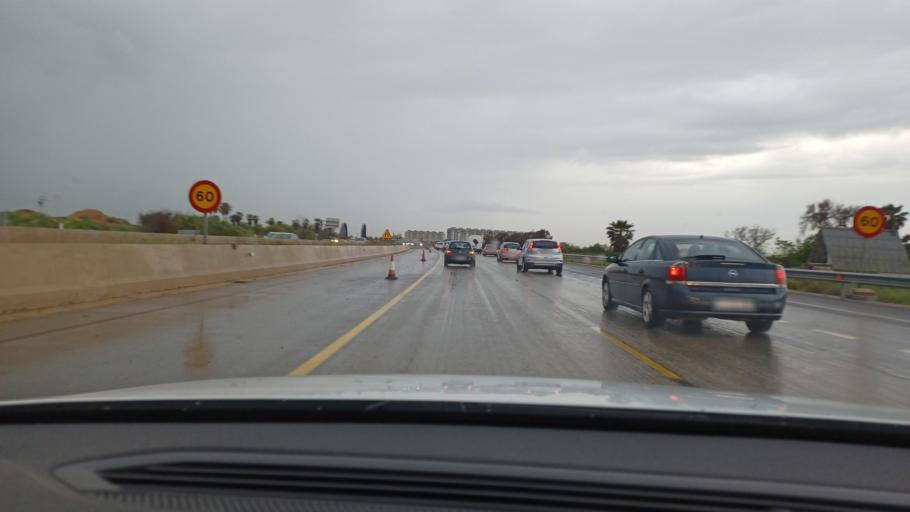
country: ES
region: Valencia
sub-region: Provincia de Valencia
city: Alboraya
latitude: 39.5052
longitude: -0.3260
